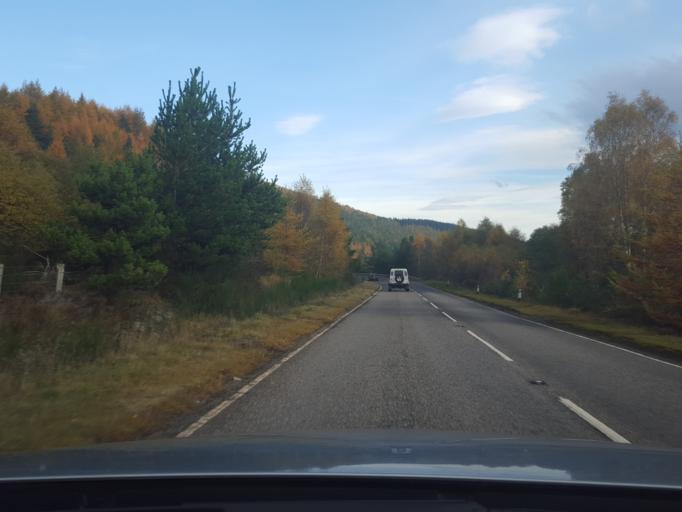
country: GB
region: Scotland
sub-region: Highland
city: Spean Bridge
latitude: 57.1985
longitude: -4.7326
